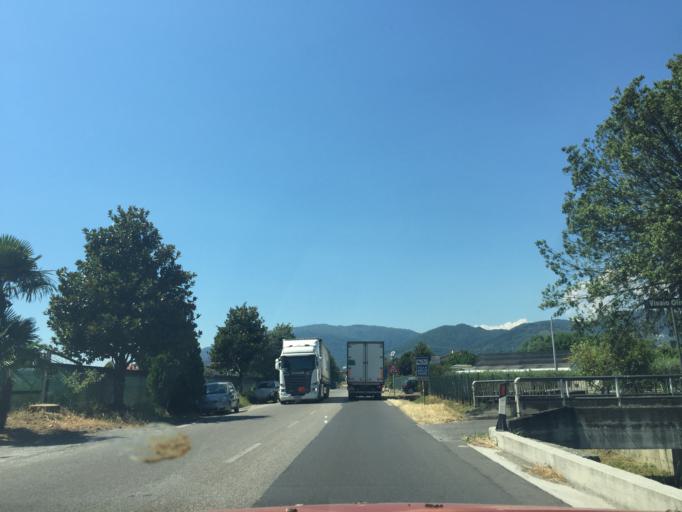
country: IT
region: Tuscany
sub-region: Provincia di Pistoia
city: Santa Lucia
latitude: 43.8712
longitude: 10.6955
